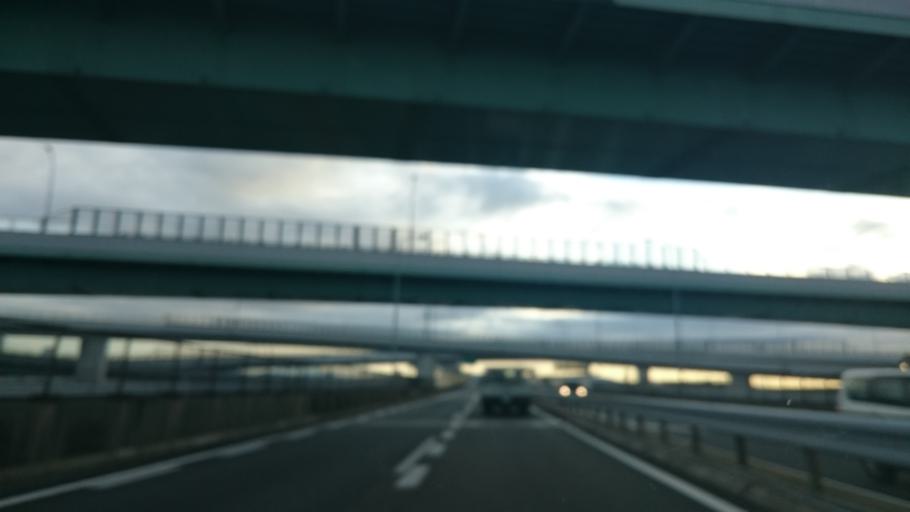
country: JP
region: Aichi
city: Iwakura
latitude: 35.2216
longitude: 136.8544
